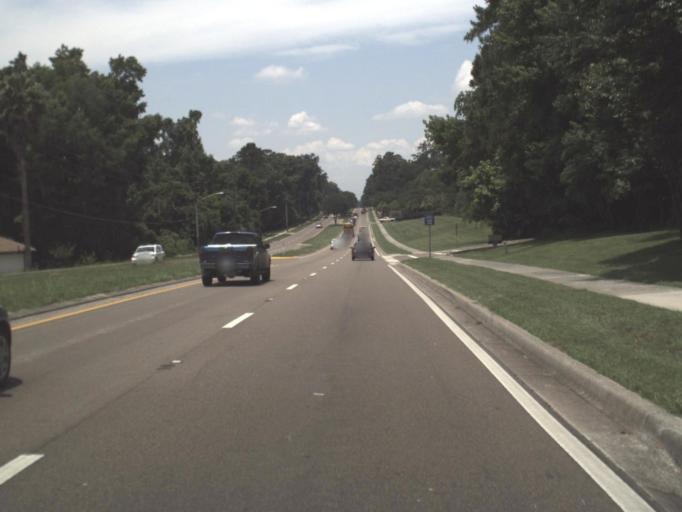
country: US
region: Florida
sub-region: Alachua County
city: Alachua
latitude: 29.6600
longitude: -82.4501
